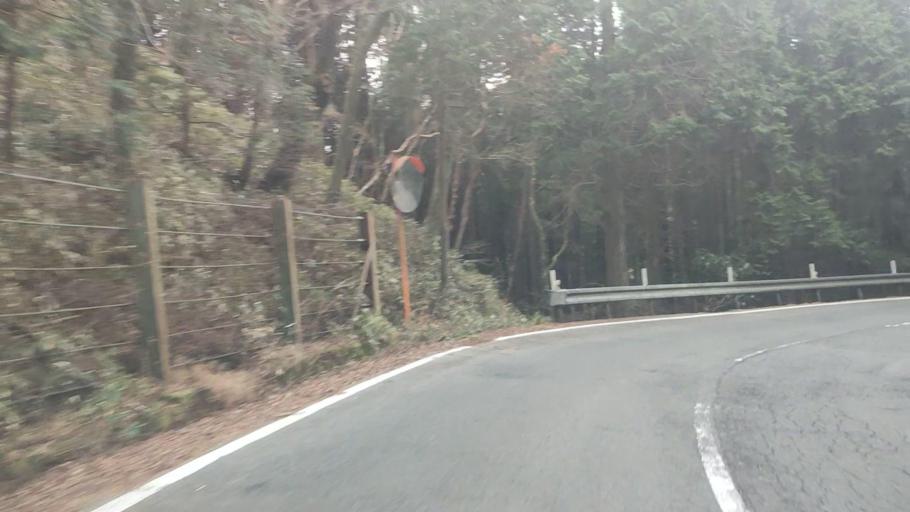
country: JP
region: Nagasaki
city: Shimabara
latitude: 32.7530
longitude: 130.2770
